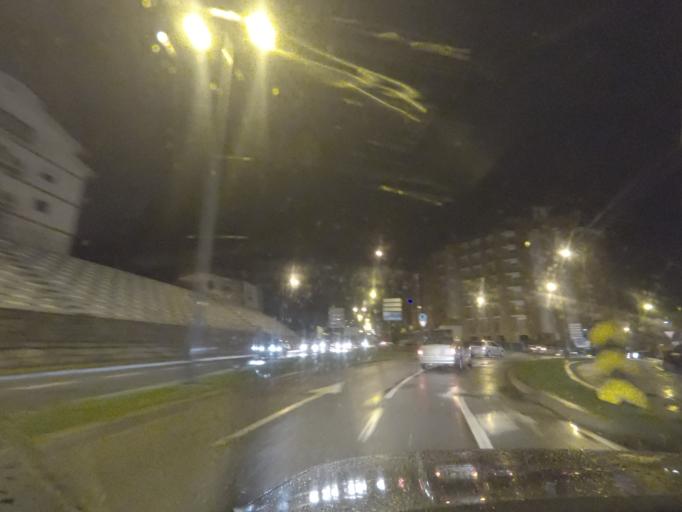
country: PT
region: Vila Real
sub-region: Vila Real
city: Vila Real
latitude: 41.3027
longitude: -7.7409
